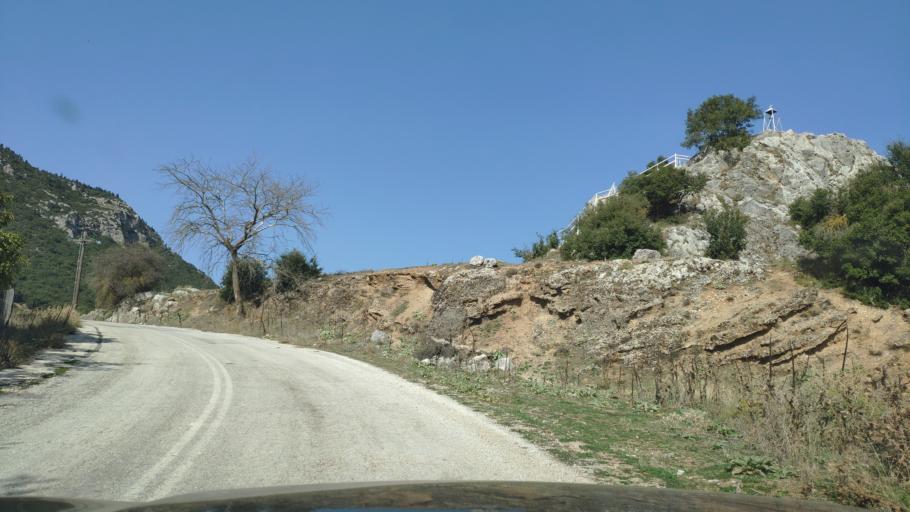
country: GR
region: West Greece
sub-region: Nomos Achaias
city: Aiyira
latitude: 37.9600
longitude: 22.3459
